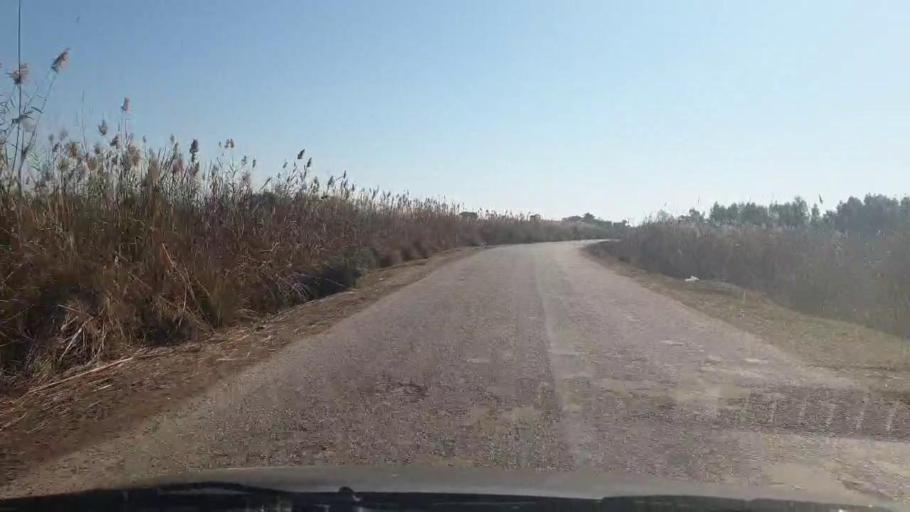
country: PK
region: Sindh
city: Bozdar
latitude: 27.1564
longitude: 68.6528
